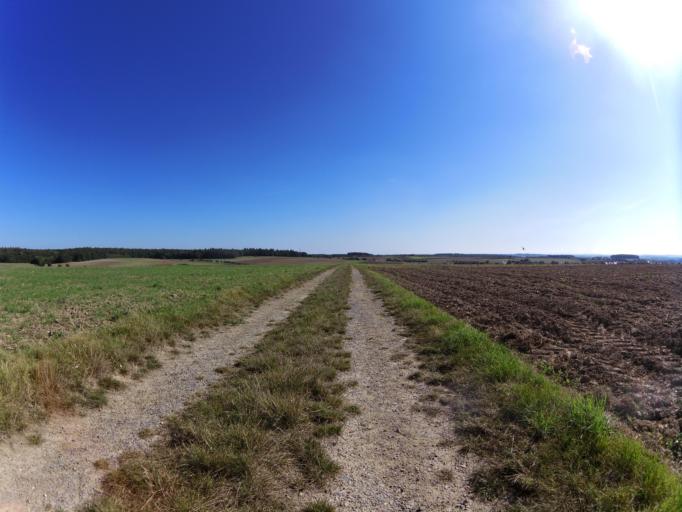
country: DE
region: Bavaria
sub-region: Regierungsbezirk Unterfranken
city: Waldbrunn
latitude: 49.7144
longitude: 9.7870
